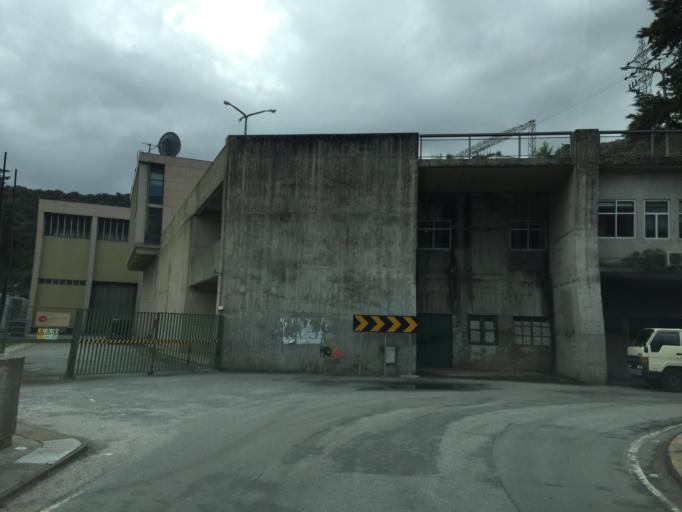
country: PT
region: Braganca
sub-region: Miranda do Douro
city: Miranda do Douro
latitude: 41.4892
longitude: -6.2647
